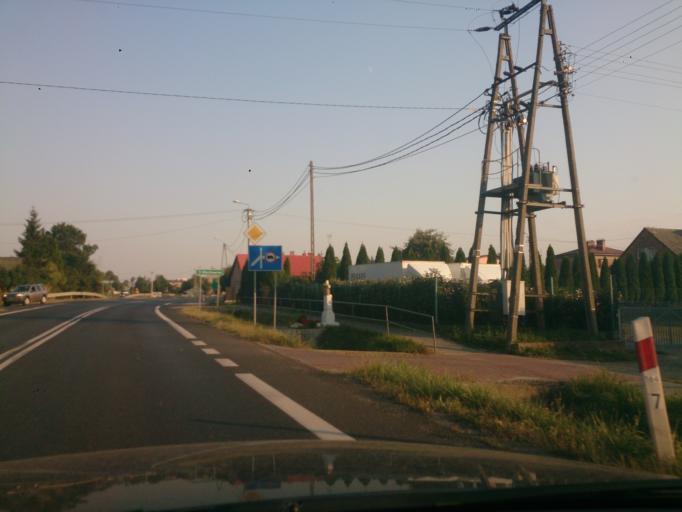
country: PL
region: Subcarpathian Voivodeship
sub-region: Powiat kolbuszowski
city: Kolbuszowa
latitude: 50.2532
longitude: 21.7722
